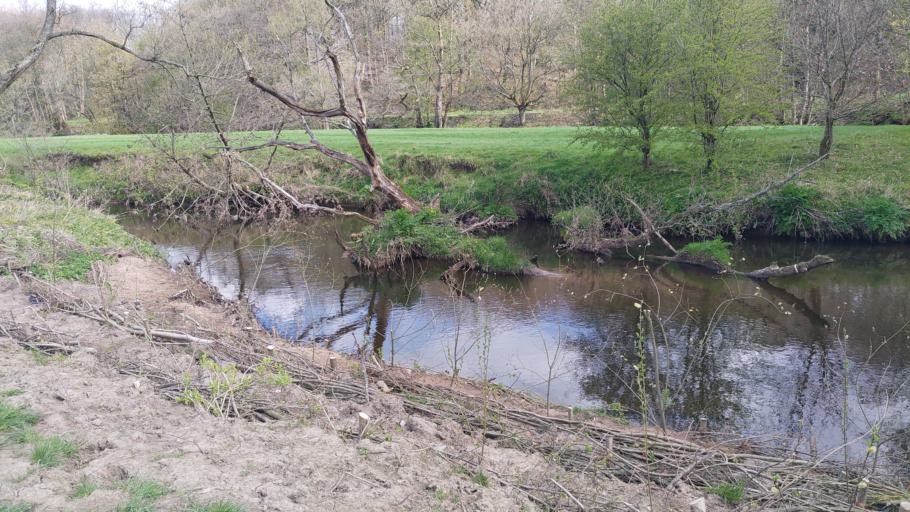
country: GB
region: England
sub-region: Lancashire
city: Coppull
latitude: 53.6472
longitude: -2.6565
